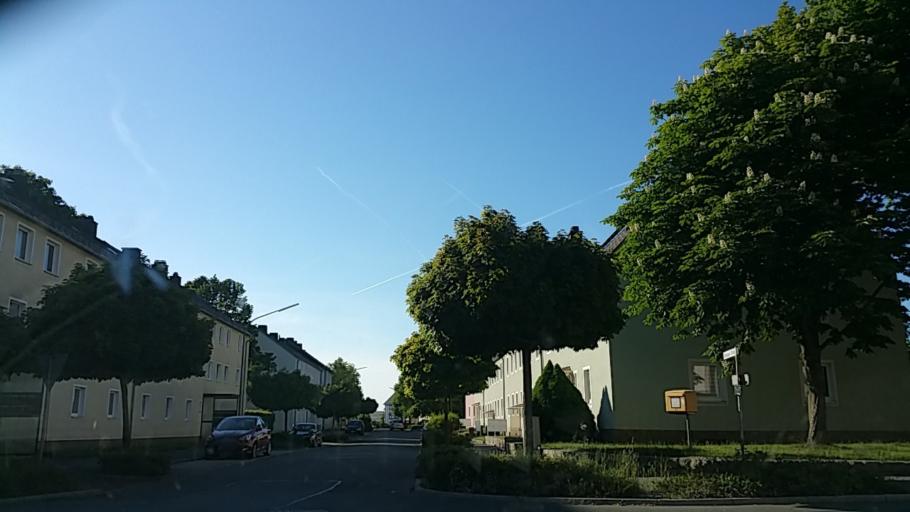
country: DE
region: Bavaria
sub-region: Upper Franconia
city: Schwarzenbach an der Saale
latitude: 50.2157
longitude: 11.9431
